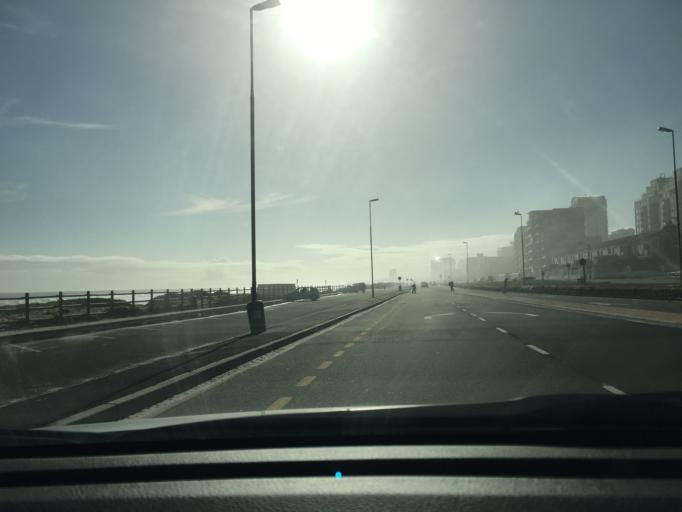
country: ZA
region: Western Cape
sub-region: City of Cape Town
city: Sunset Beach
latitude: -33.8207
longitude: 18.4758
